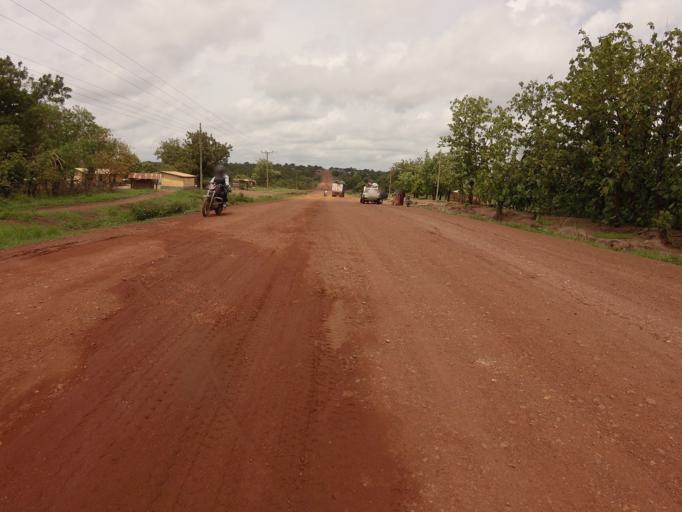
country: GH
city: Kpandae
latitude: 8.4766
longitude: 0.3230
